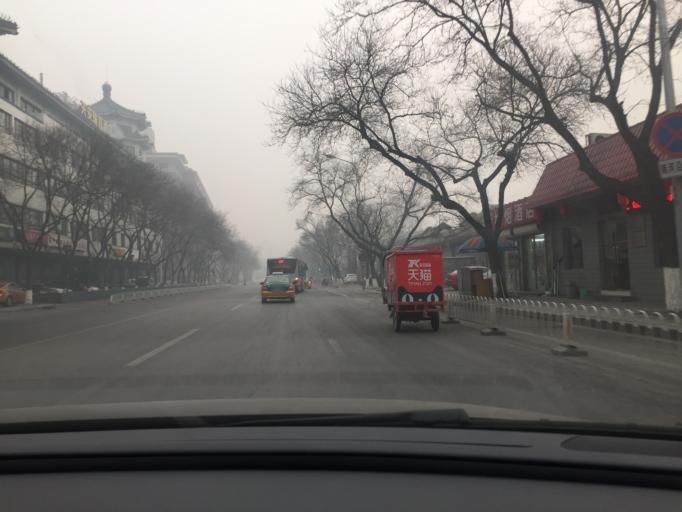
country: CN
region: Beijing
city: Beijing
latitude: 39.9094
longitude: 116.4005
